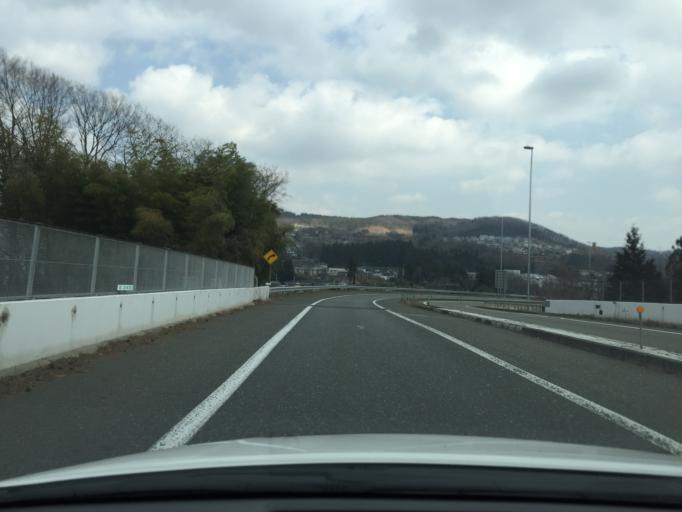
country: JP
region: Miyagi
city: Sendai
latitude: 38.2601
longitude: 140.8149
